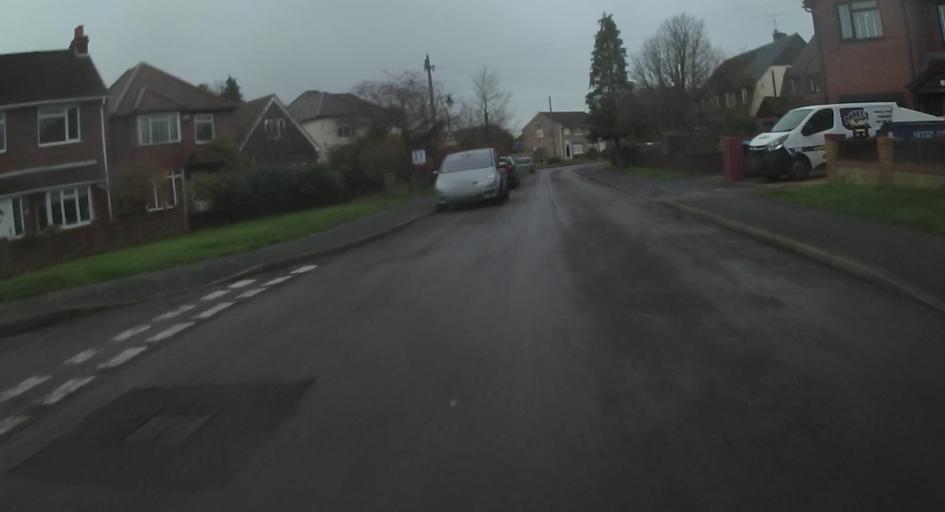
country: GB
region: England
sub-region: Surrey
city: Frimley
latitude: 51.3027
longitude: -0.7309
